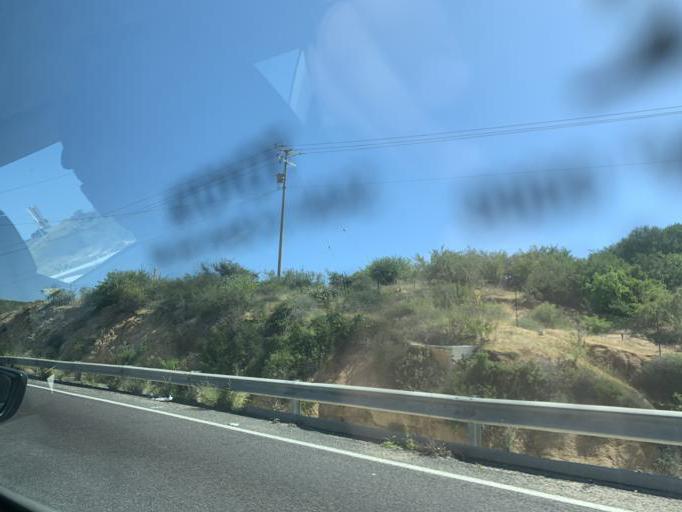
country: MX
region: Baja California Sur
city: Cabo San Lucas
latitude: 22.9631
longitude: -109.8003
